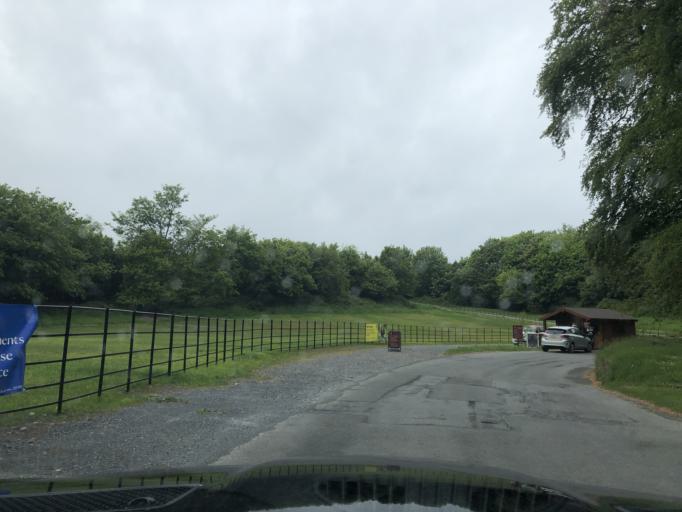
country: GB
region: Northern Ireland
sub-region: Down District
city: Portaferry
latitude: 54.3671
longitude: -5.5844
